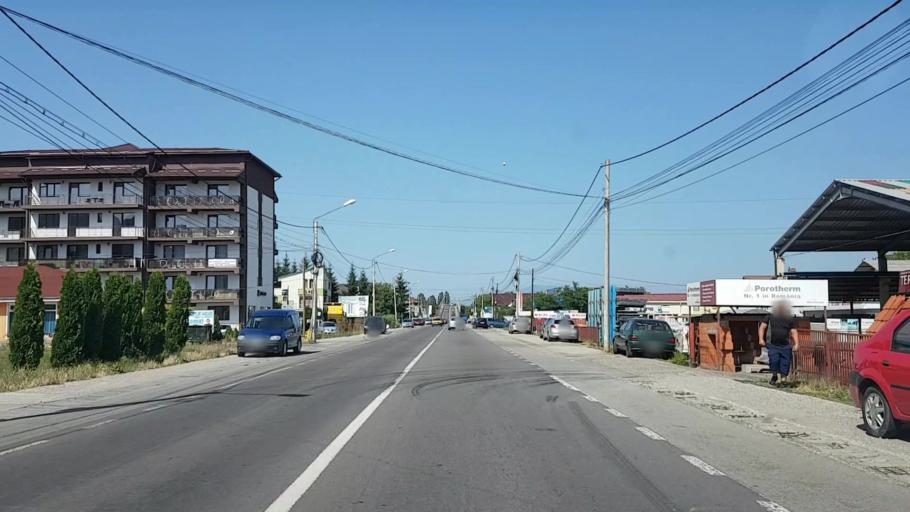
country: RO
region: Bistrita-Nasaud
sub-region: Municipiul Bistrita
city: Viisoara
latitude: 47.1125
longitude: 24.4609
